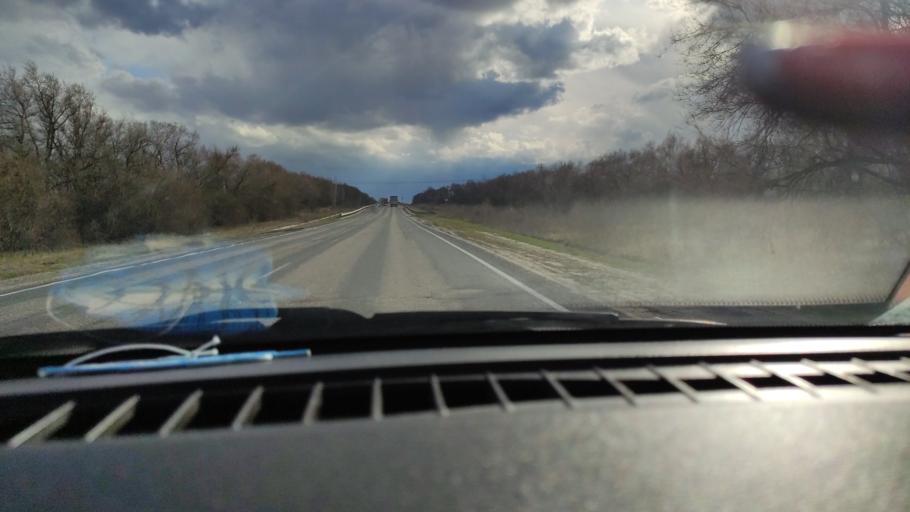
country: RU
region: Saratov
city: Sinodskoye
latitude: 51.9623
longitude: 46.6266
